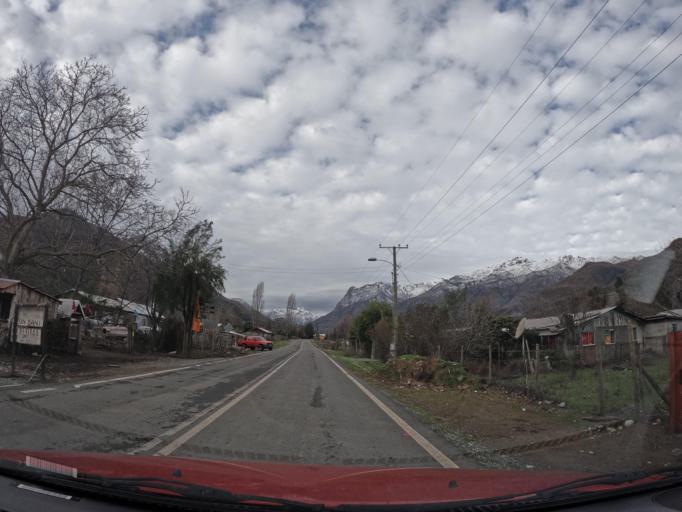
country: CL
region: Maule
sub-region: Provincia de Linares
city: Colbun
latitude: -35.8605
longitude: -71.2632
